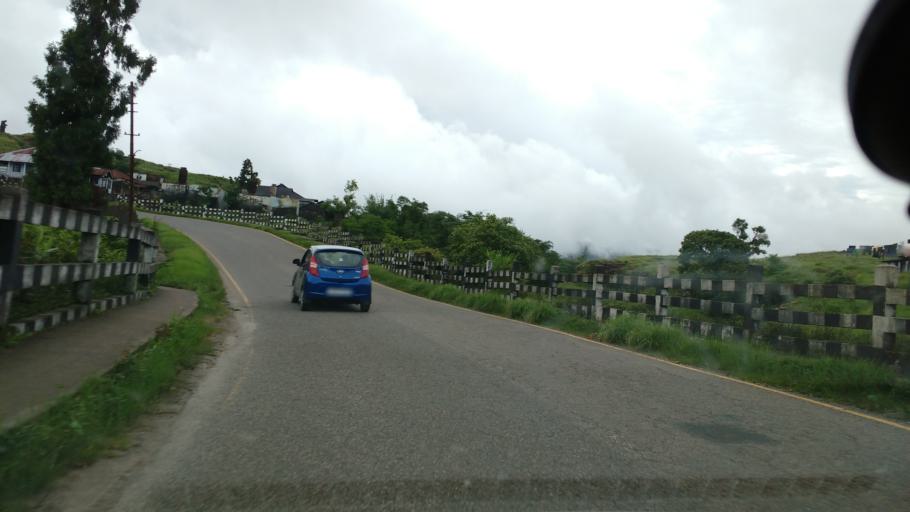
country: IN
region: Meghalaya
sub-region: East Khasi Hills
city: Cherrapunji
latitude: 25.2758
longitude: 91.7308
